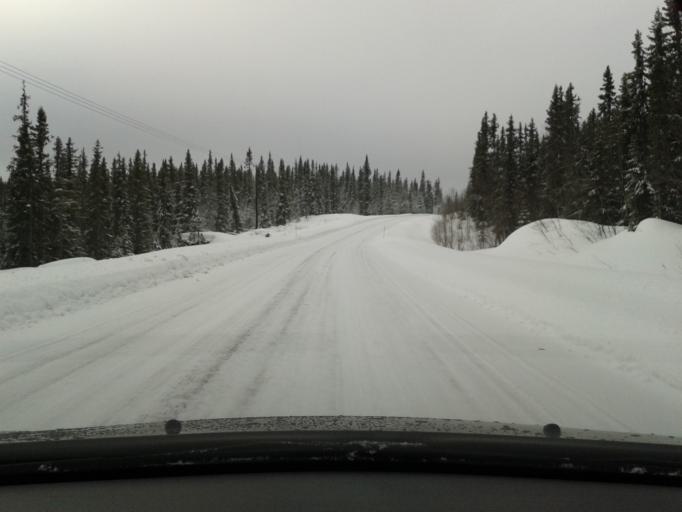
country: SE
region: Vaesterbotten
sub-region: Vilhelmina Kommun
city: Sjoberg
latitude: 65.1887
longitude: 15.9444
